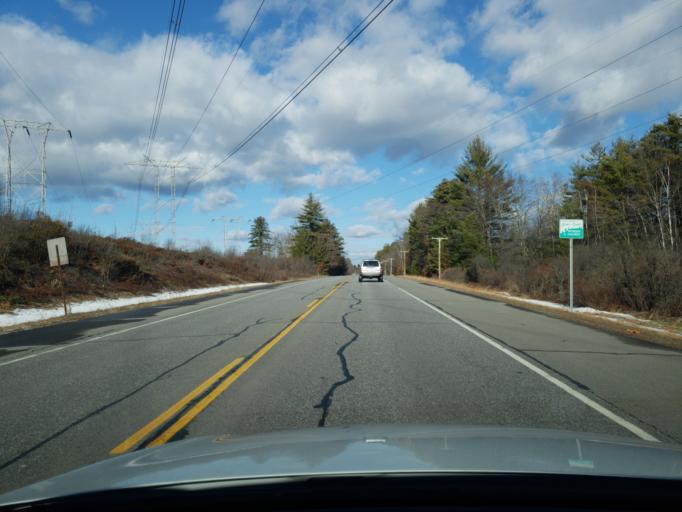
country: US
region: New Hampshire
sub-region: Hillsborough County
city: Pinardville
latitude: 42.9830
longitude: -71.5207
